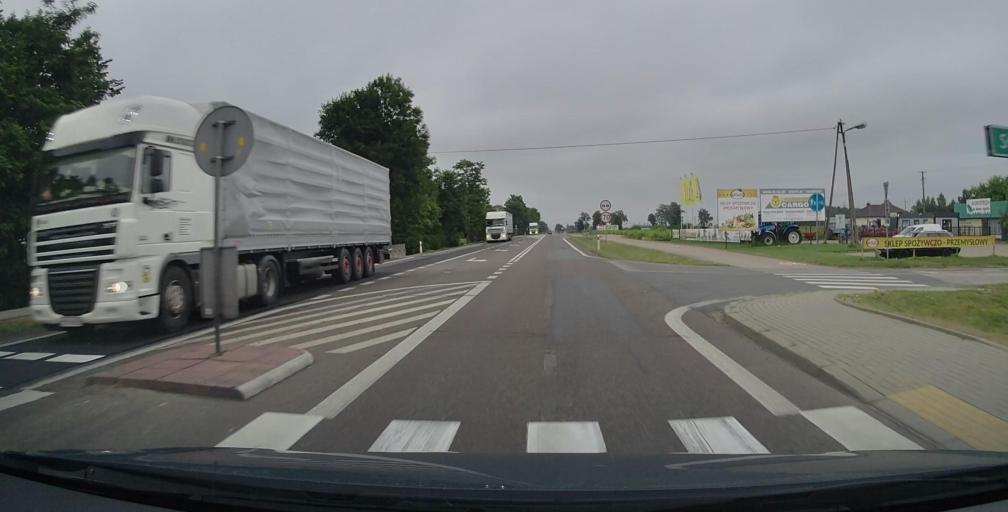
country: PL
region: Lublin Voivodeship
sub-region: Powiat bialski
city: Lesna Podlaska
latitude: 52.0361
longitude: 23.0043
